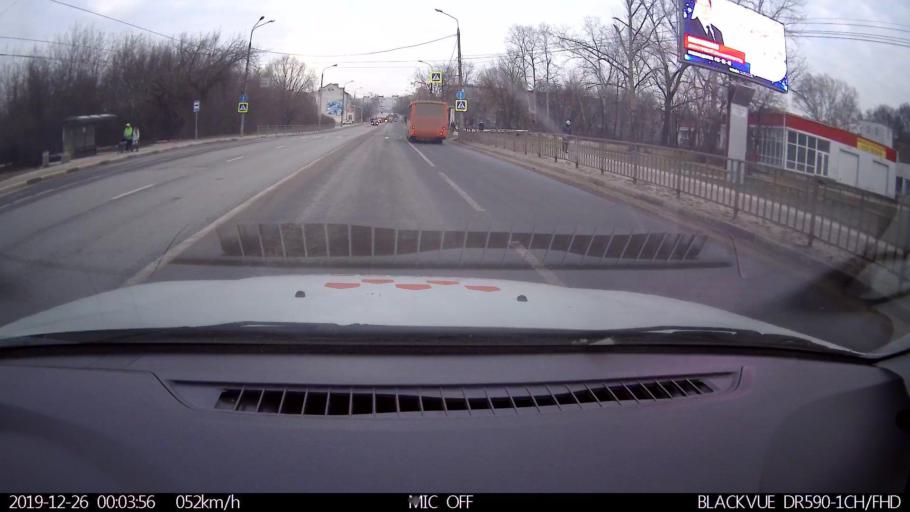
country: RU
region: Nizjnij Novgorod
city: Gorbatovka
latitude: 56.3454
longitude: 43.8427
